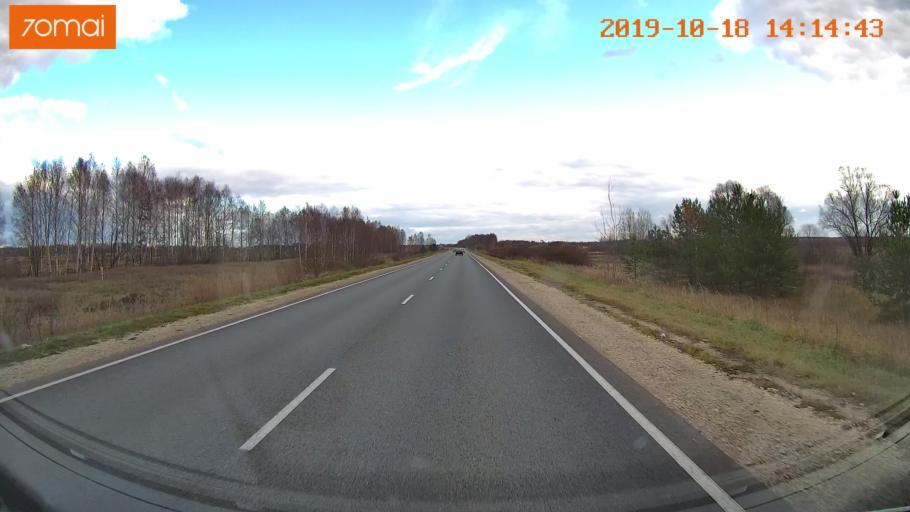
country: RU
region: Rjazan
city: Spas-Klepiki
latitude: 55.1490
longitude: 40.3015
